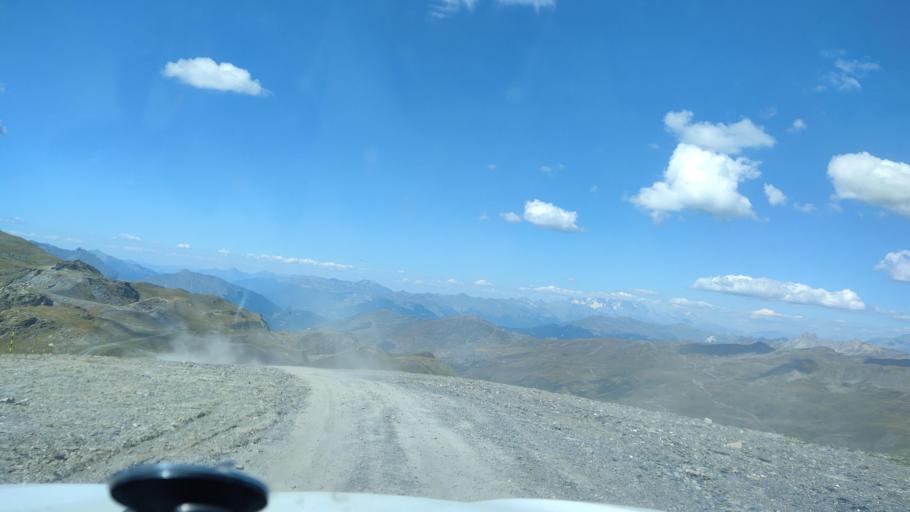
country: FR
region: Rhone-Alpes
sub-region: Departement de la Savoie
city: Val Thorens
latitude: 45.3016
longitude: 6.5064
